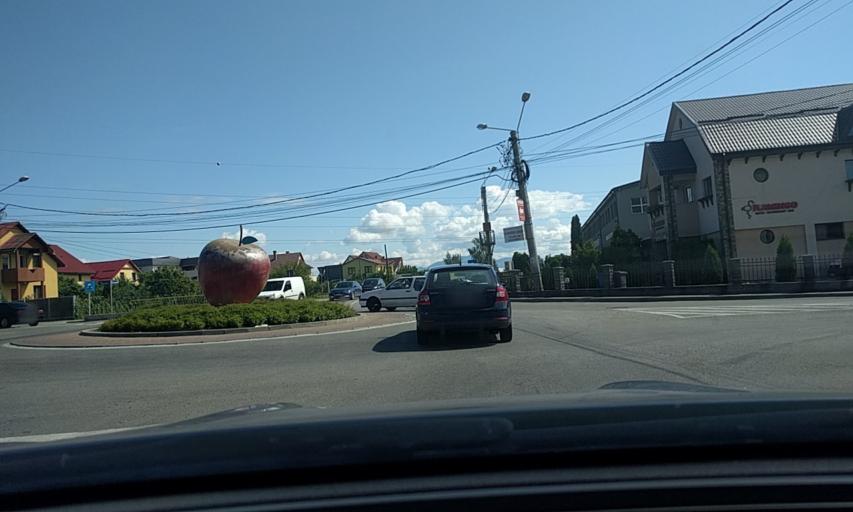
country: RO
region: Bistrita-Nasaud
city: Bistrita
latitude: 47.1466
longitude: 24.4907
